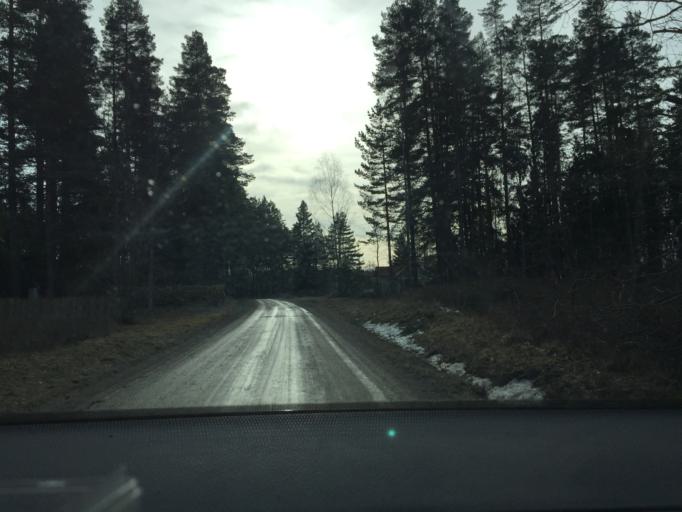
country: SE
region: OErebro
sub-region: Orebro Kommun
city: Odensbacken
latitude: 59.1286
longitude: 15.4741
